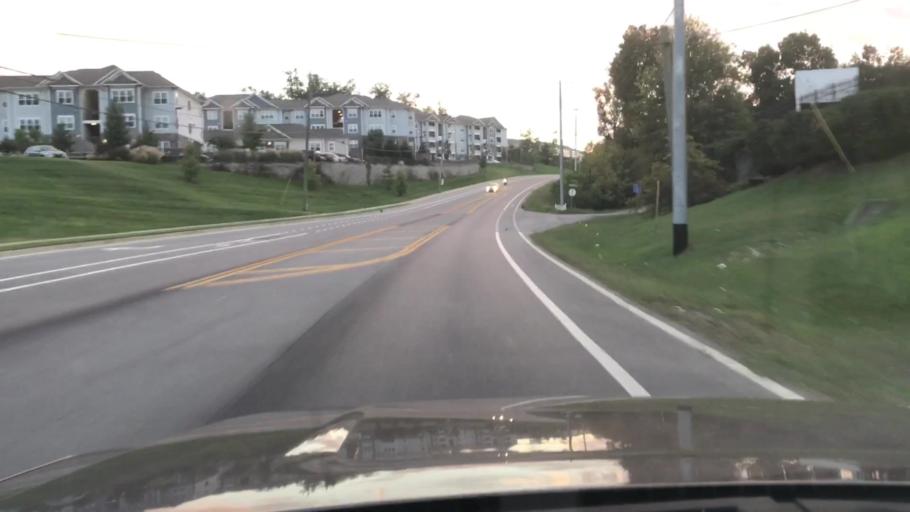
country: US
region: Tennessee
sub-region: Davidson County
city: Belle Meade
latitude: 36.1243
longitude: -86.9105
